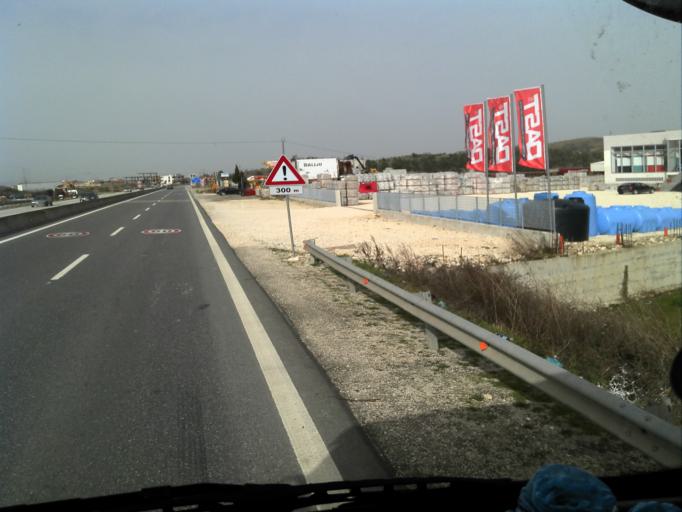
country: AL
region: Tirane
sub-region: Rrethi i Kavajes
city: Rrogozhine
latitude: 41.0681
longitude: 19.6419
